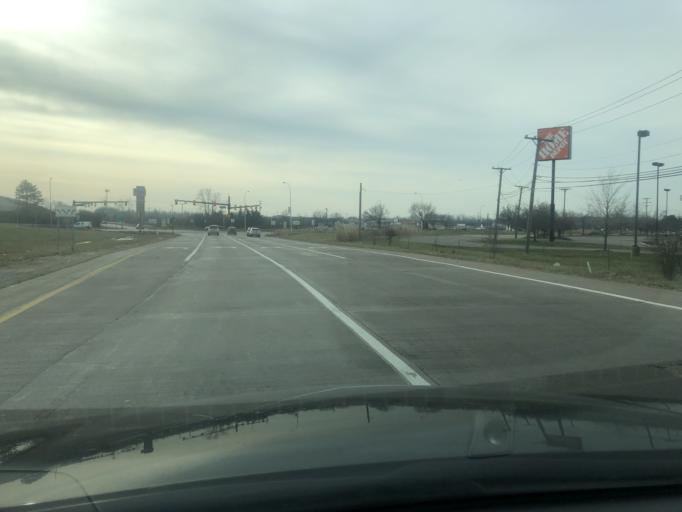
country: US
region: Michigan
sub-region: Wayne County
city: Southgate
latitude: 42.1994
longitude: -83.2395
